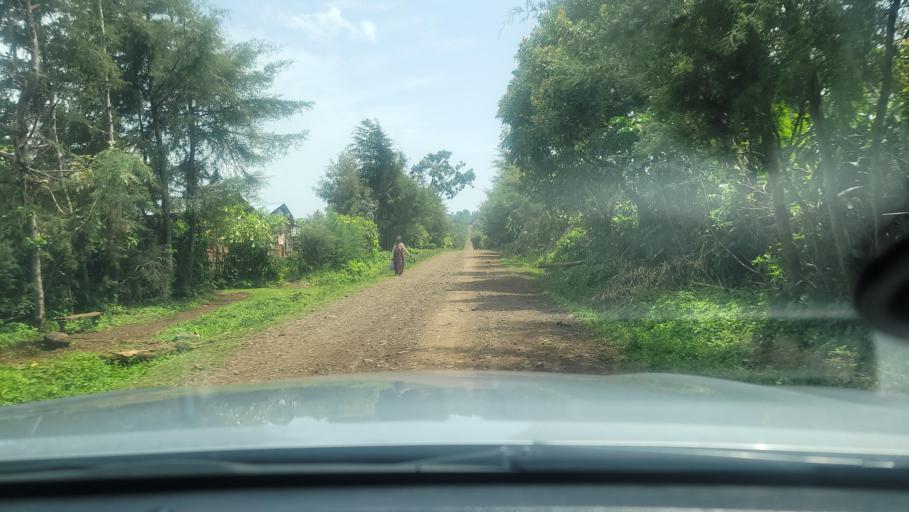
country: ET
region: Oromiya
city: Agaro
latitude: 7.8226
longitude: 36.4081
